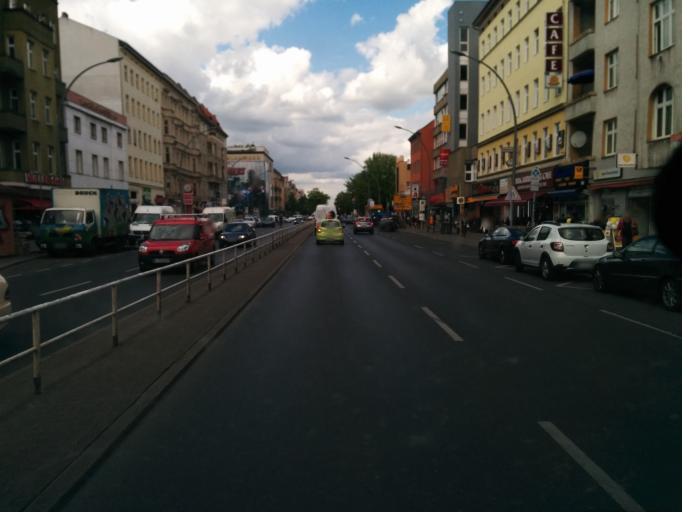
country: DE
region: Berlin
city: Wedding Bezirk
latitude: 52.5495
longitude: 13.3539
